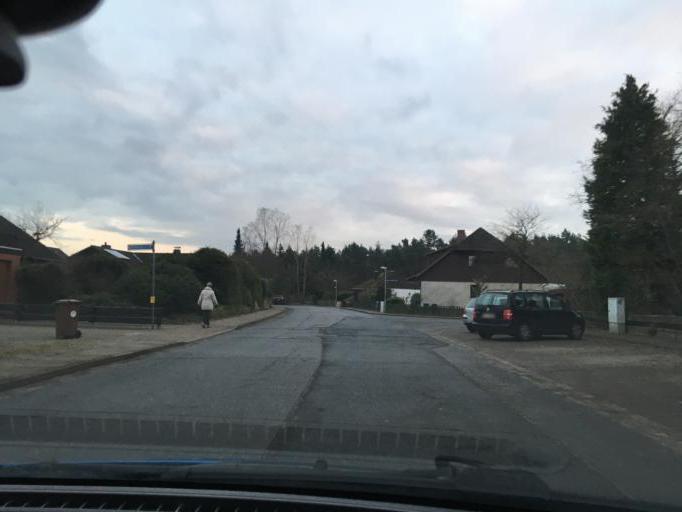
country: DE
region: Lower Saxony
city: Wendisch Evern
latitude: 53.2286
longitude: 10.4443
